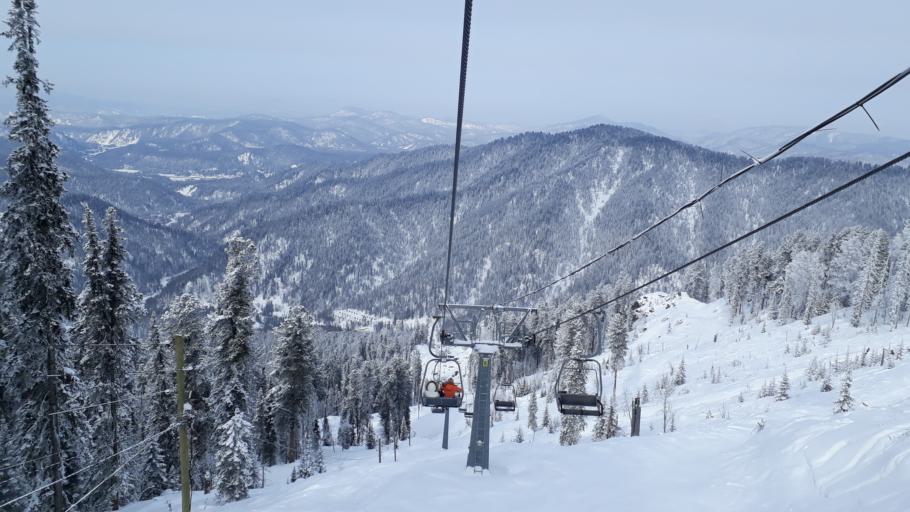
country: RU
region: Altay
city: Iogach
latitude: 51.7313
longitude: 87.3000
